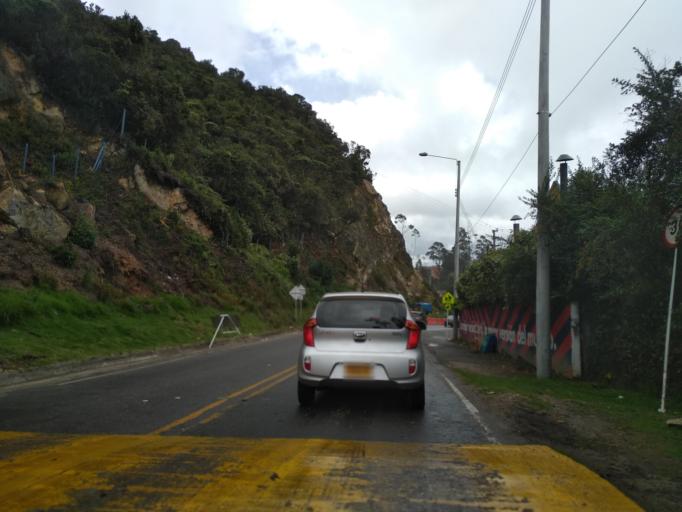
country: CO
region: Bogota D.C.
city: Barrio San Luis
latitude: 4.6721
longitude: -73.9963
